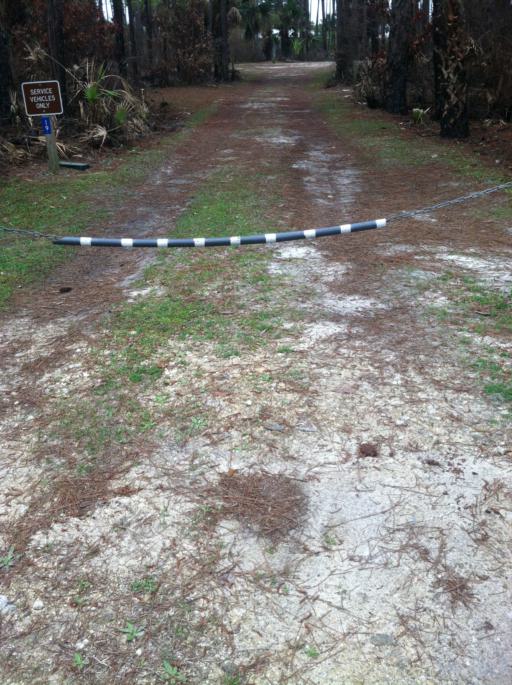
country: US
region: Florida
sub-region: Gulf County
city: Port Saint Joe
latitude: 29.7800
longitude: -85.4062
